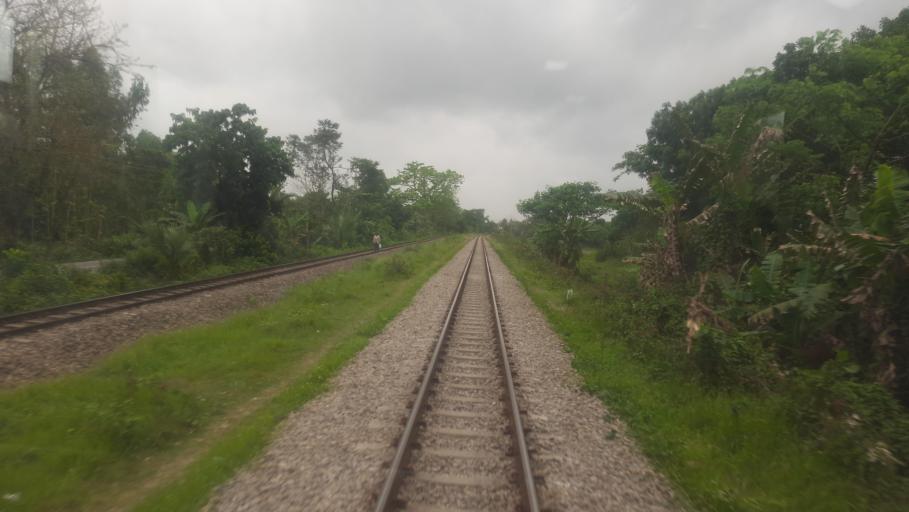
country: BD
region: Dhaka
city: Narsingdi
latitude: 23.9392
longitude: 90.7791
